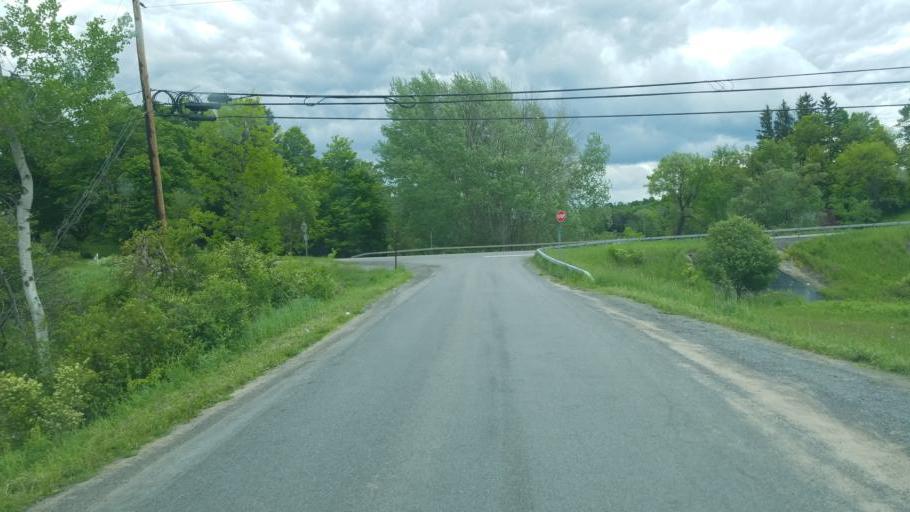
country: US
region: New York
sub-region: Herkimer County
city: Ilion
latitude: 42.9115
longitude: -75.1225
